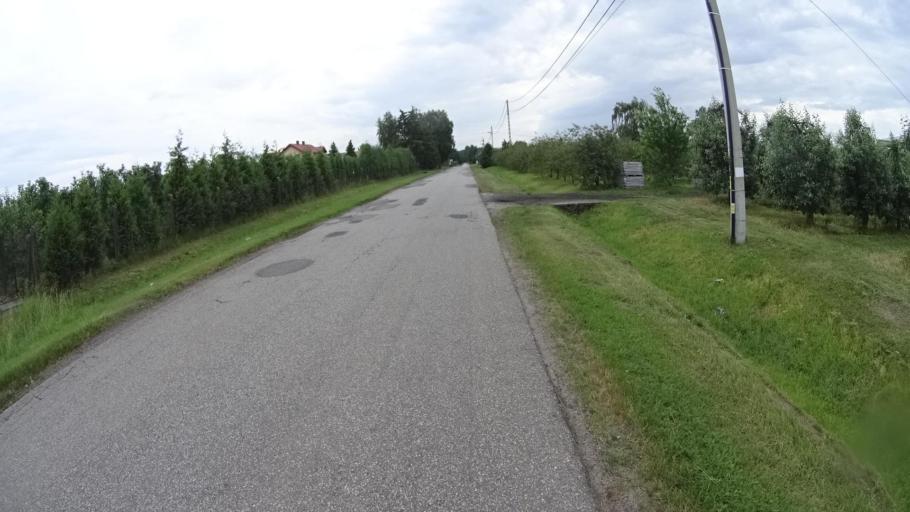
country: PL
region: Masovian Voivodeship
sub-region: Powiat grojecki
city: Goszczyn
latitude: 51.7906
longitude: 20.8567
